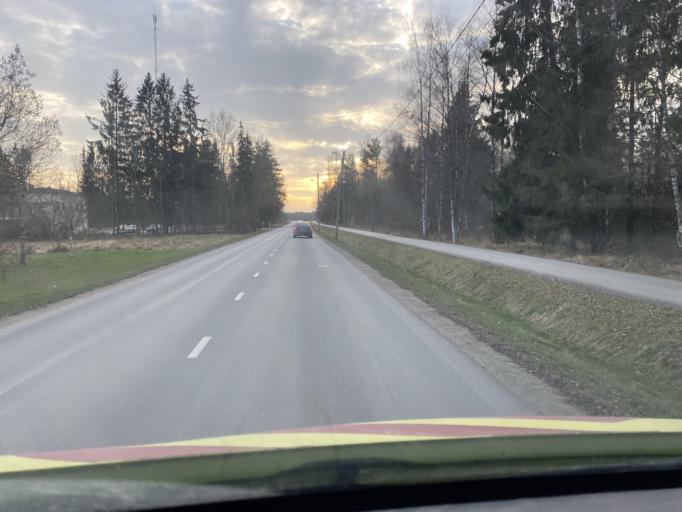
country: EE
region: Jogevamaa
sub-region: Poltsamaa linn
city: Poltsamaa
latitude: 58.6425
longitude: 25.9775
